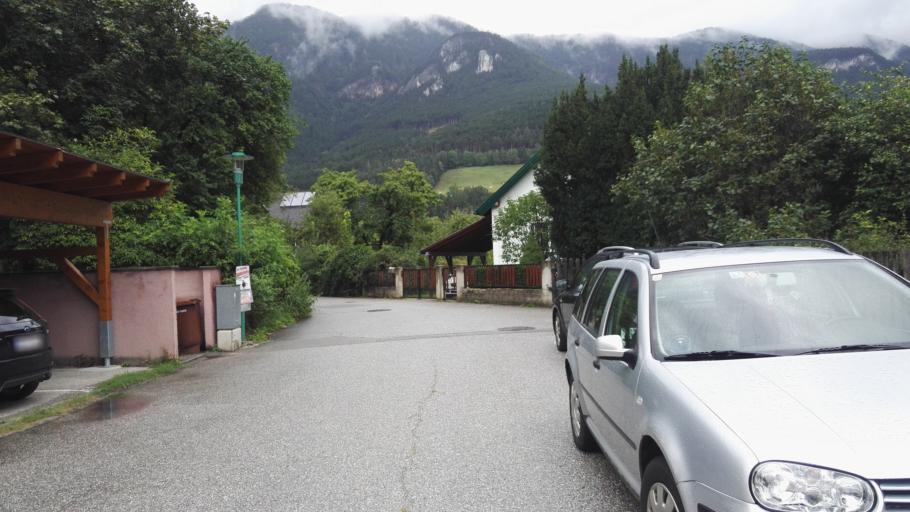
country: AT
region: Lower Austria
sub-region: Politischer Bezirk Neunkirchen
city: Payerbach
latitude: 47.6906
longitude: 15.8666
